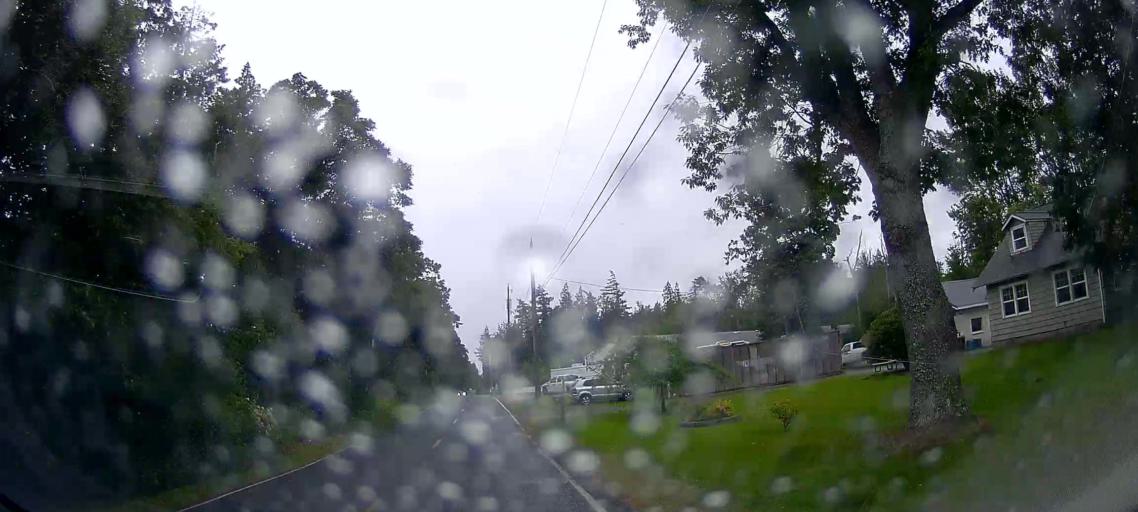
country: US
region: Washington
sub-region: Whatcom County
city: Marietta
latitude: 48.8020
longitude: -122.5748
